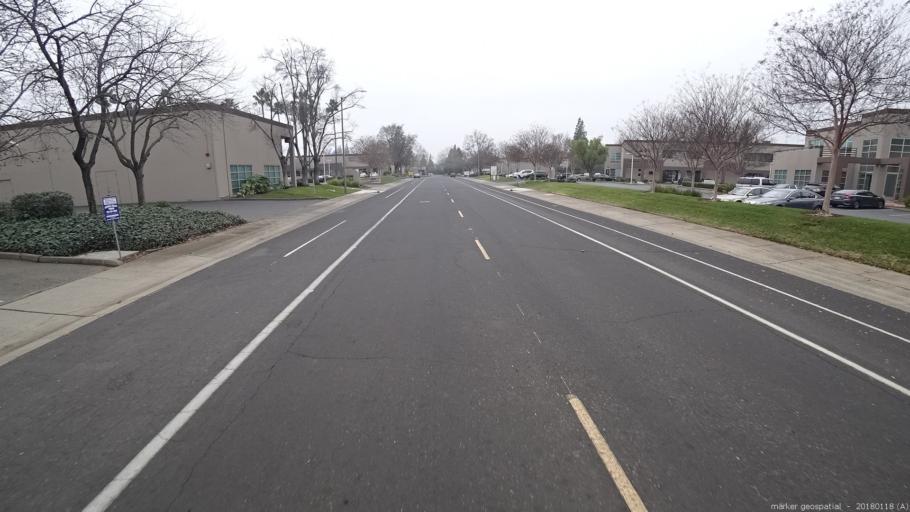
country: US
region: California
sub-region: Sacramento County
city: Rancho Cordova
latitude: 38.5739
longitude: -121.3235
